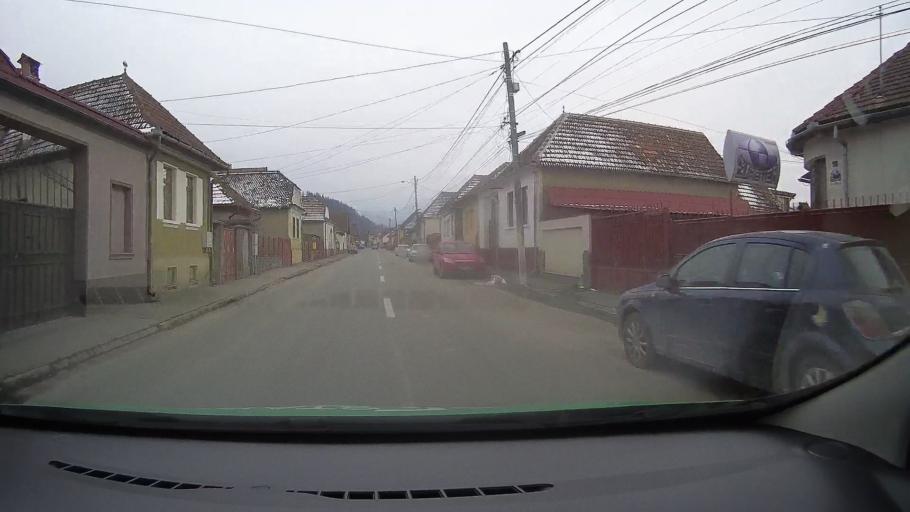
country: RO
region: Brasov
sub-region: Oras Rasnov
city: Rasnov
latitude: 45.5886
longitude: 25.4585
